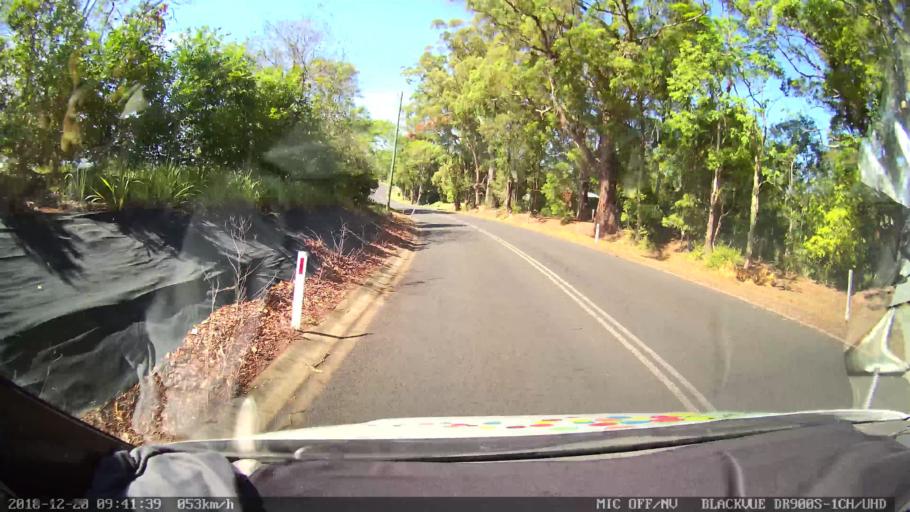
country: AU
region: New South Wales
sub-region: Lismore Municipality
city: Lismore
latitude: -28.7104
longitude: 153.2991
